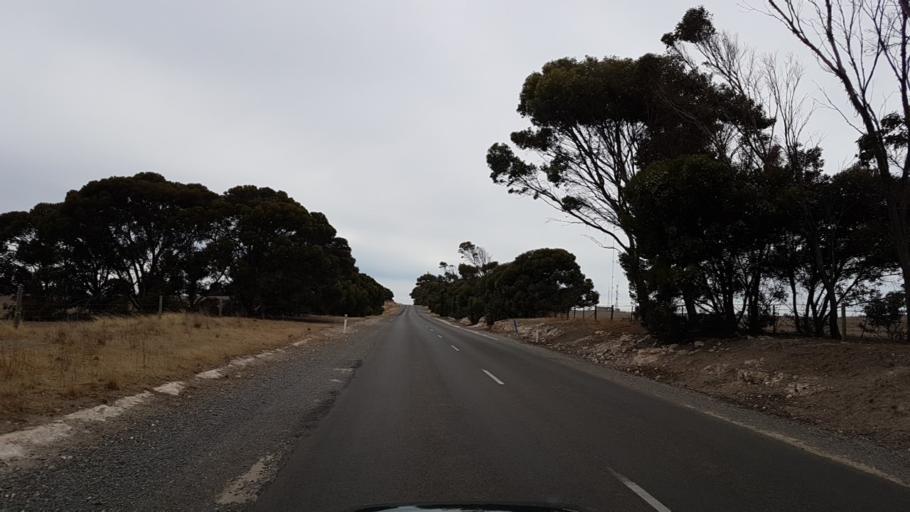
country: AU
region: South Australia
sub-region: Yorke Peninsula
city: Honiton
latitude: -34.9850
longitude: 137.2567
